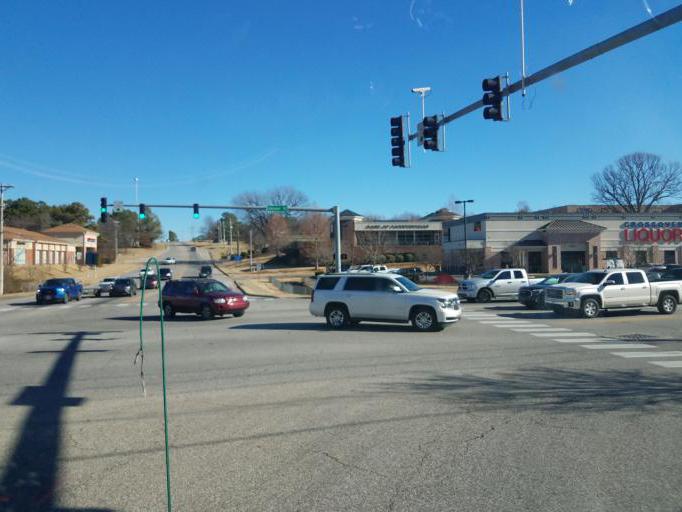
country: US
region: Arkansas
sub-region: Washington County
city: Fayetteville
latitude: 36.0873
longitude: -94.1216
